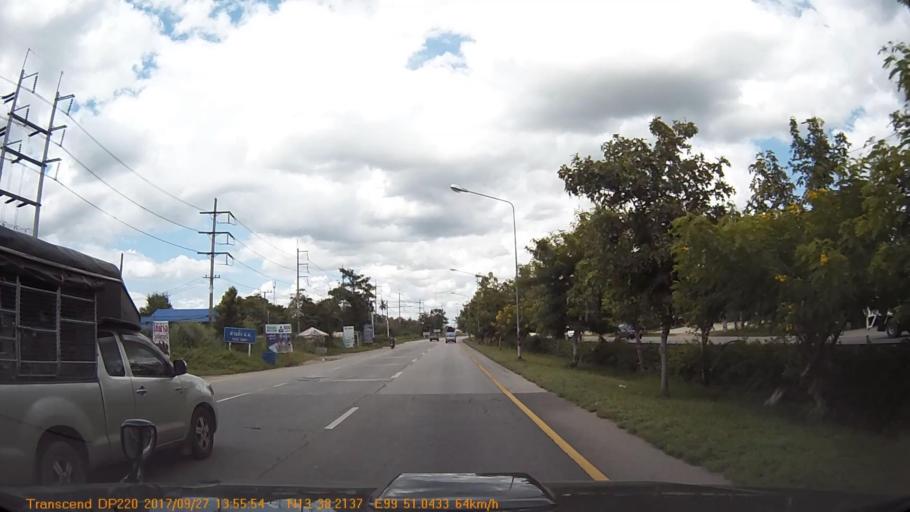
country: TH
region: Ratchaburi
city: Photharam
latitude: 13.6368
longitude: 99.8507
